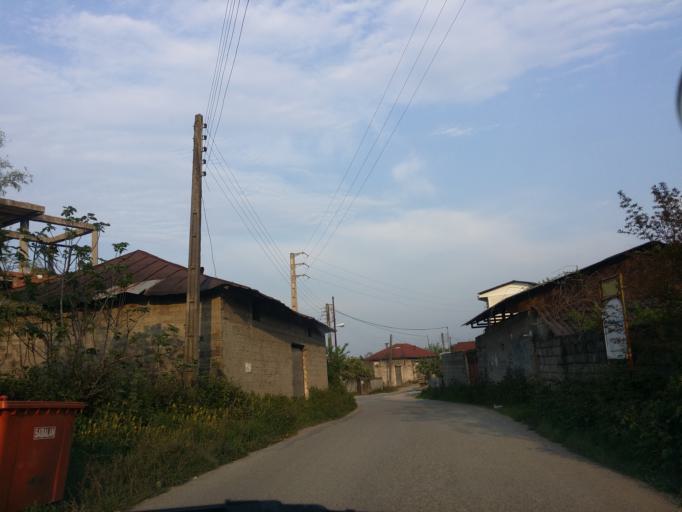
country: IR
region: Mazandaran
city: Chalus
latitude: 36.6656
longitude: 51.3736
